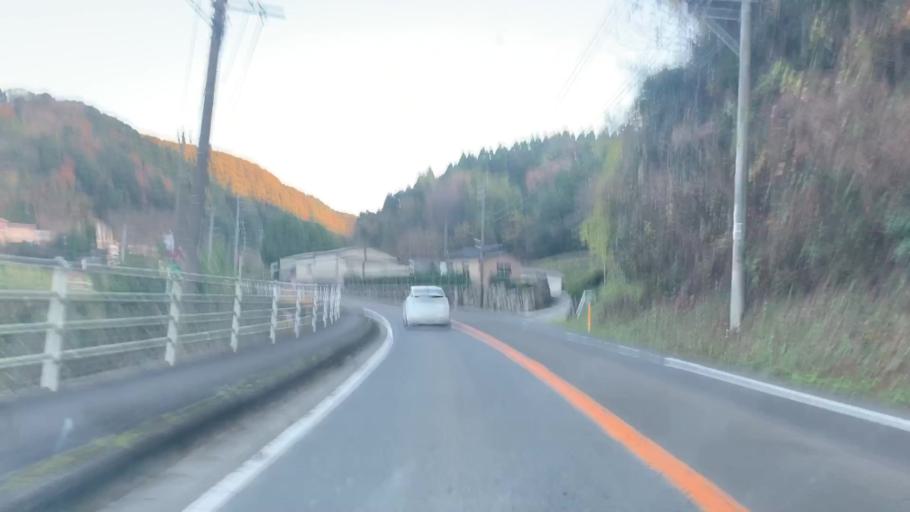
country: JP
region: Saga Prefecture
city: Takeocho-takeo
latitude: 33.2424
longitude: 130.0077
